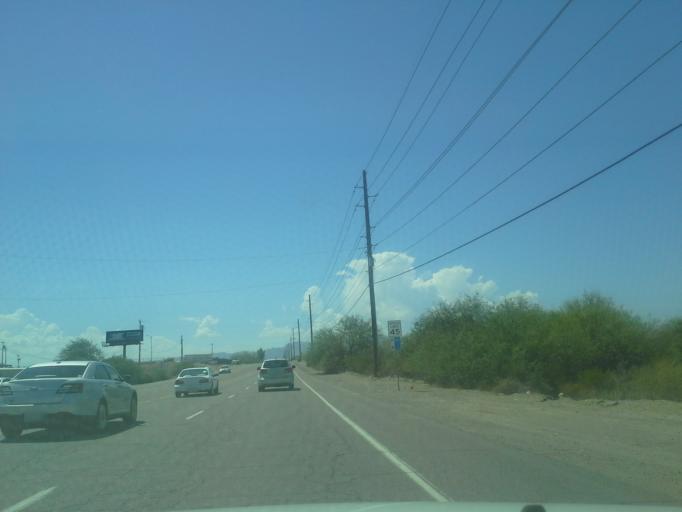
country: US
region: Arizona
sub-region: Maricopa County
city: Litchfield Park
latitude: 33.5366
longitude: -112.3242
